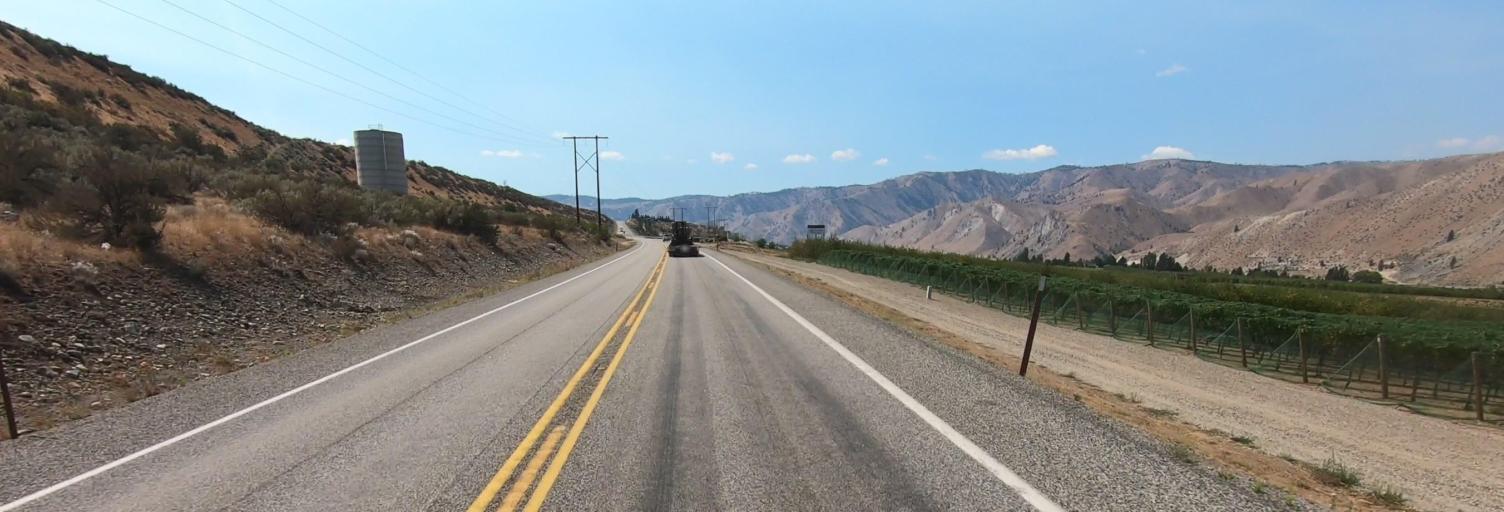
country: US
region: Washington
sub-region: Chelan County
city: Entiat
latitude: 47.7662
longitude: -120.1414
